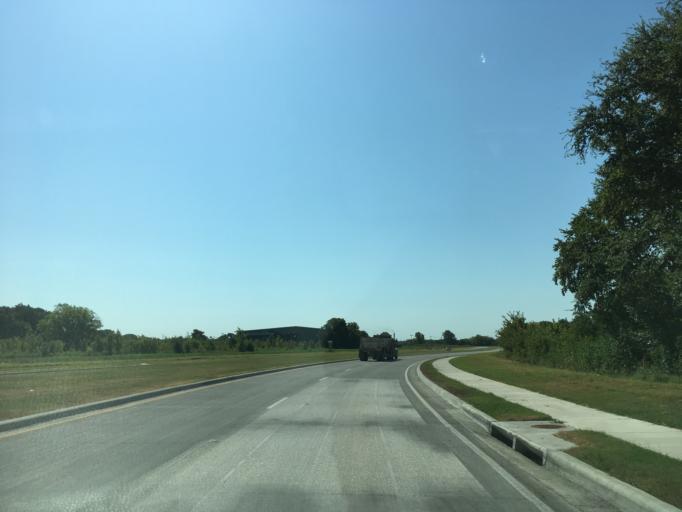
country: US
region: Texas
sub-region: Collin County
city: Fairview
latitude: 33.1701
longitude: -96.6058
